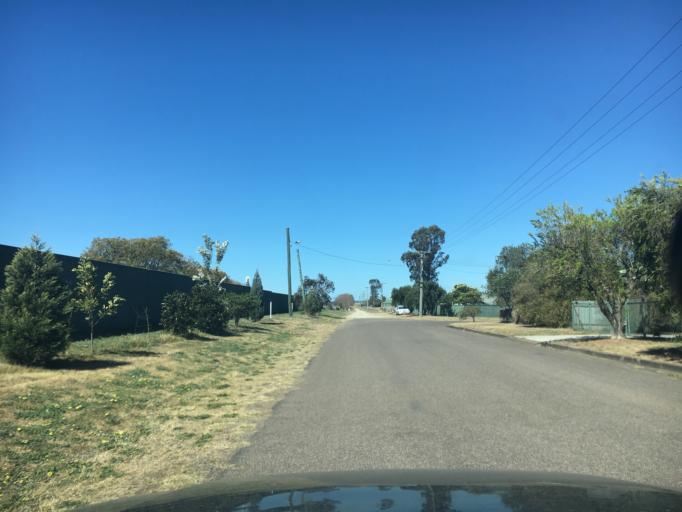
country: AU
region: New South Wales
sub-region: Singleton
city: Singleton
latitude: -32.5756
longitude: 151.1698
